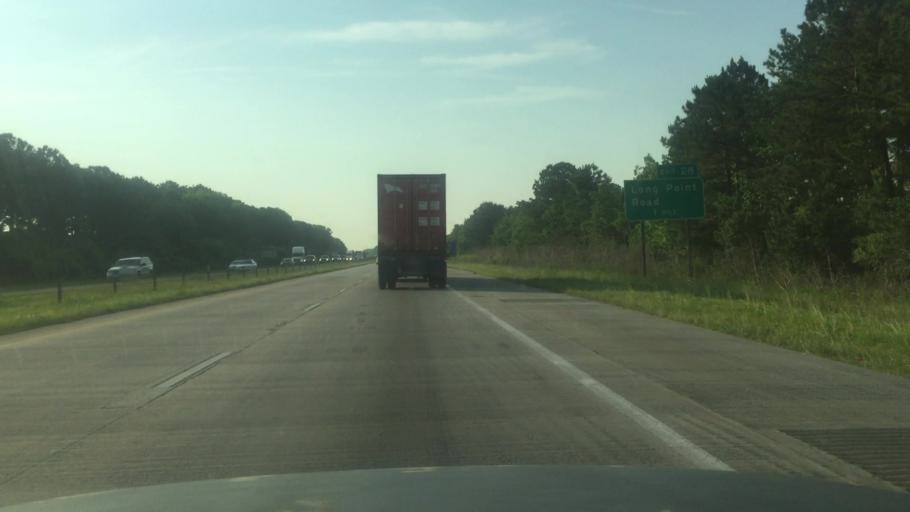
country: US
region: South Carolina
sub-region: Charleston County
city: Mount Pleasant
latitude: 32.8498
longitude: -79.8808
